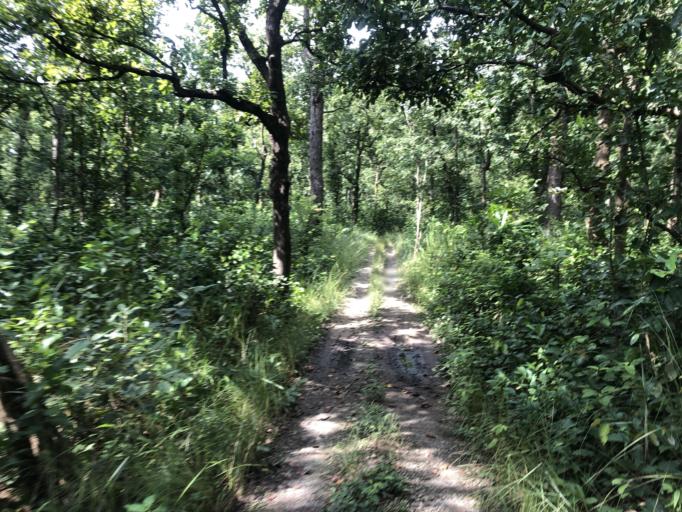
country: NP
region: Far Western
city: Tikapur
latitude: 28.5454
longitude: 81.2864
